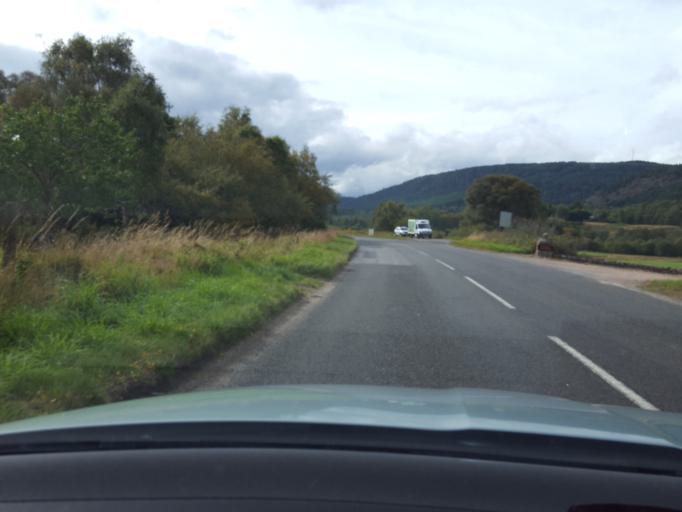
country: GB
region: Scotland
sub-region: Aberdeenshire
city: Ballater
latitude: 57.0685
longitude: -2.9886
